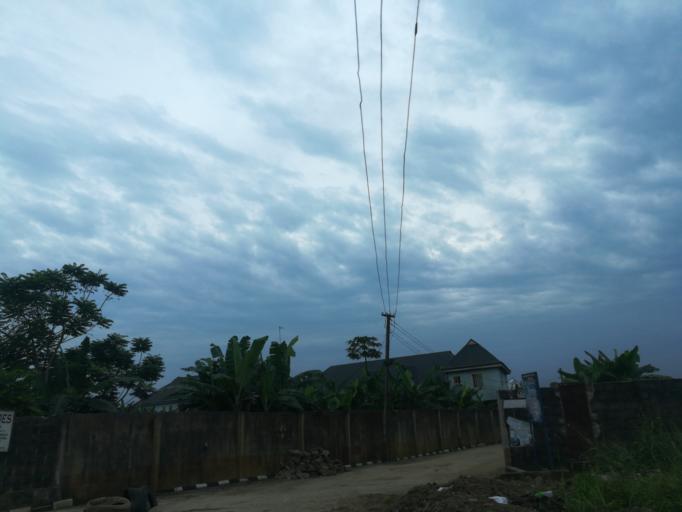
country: NG
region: Rivers
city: Port Harcourt
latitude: 4.7966
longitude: 6.9545
